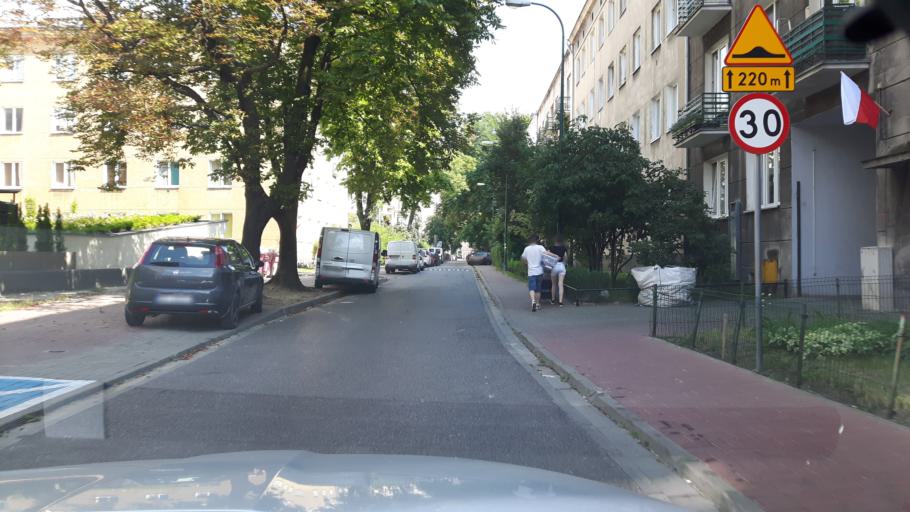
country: PL
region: Masovian Voivodeship
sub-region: Warszawa
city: Ochota
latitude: 52.2136
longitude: 20.9741
